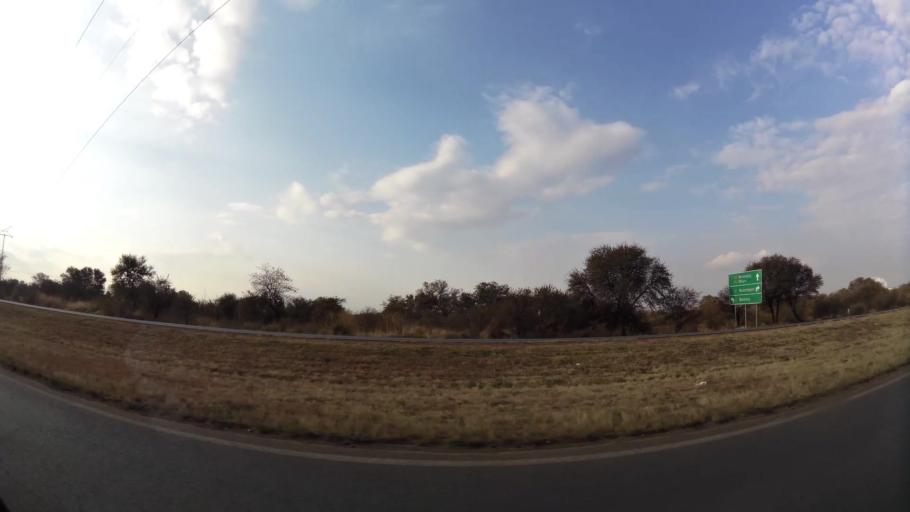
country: ZA
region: Gauteng
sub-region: Sedibeng District Municipality
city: Vanderbijlpark
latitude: -26.6210
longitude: 27.8483
